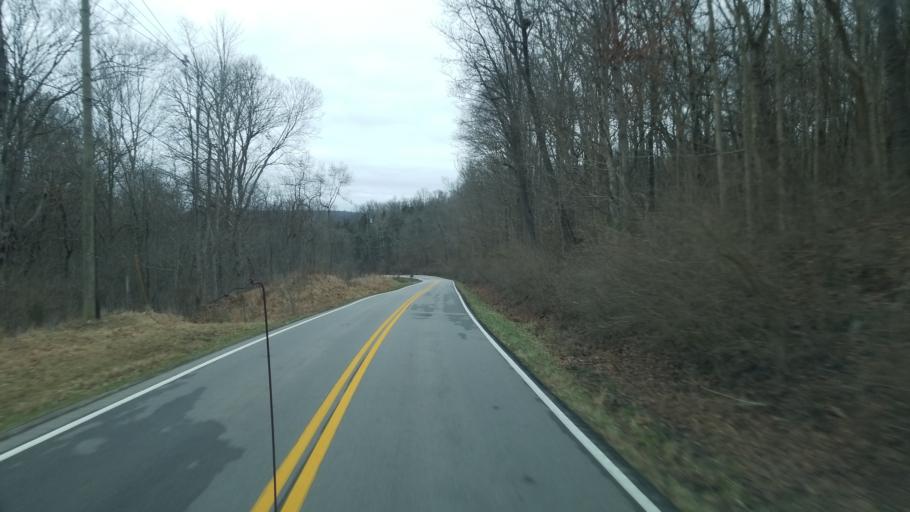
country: US
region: Ohio
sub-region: Clermont County
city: New Richmond
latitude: 38.8723
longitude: -84.2438
